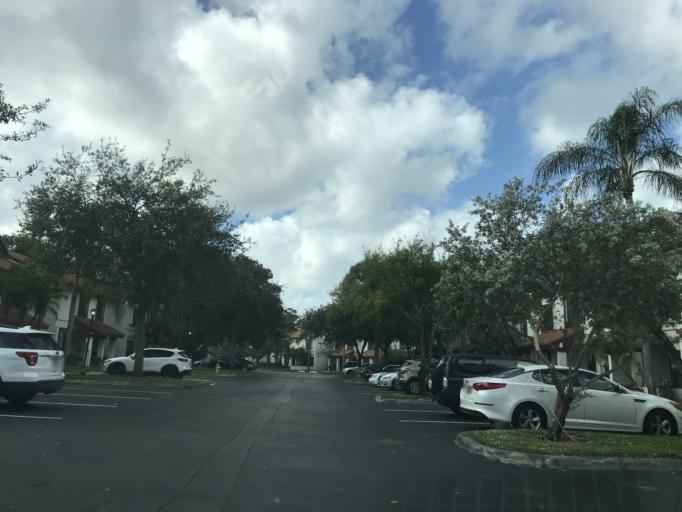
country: US
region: Florida
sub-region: Broward County
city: Coconut Creek
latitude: 26.2725
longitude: -80.1893
